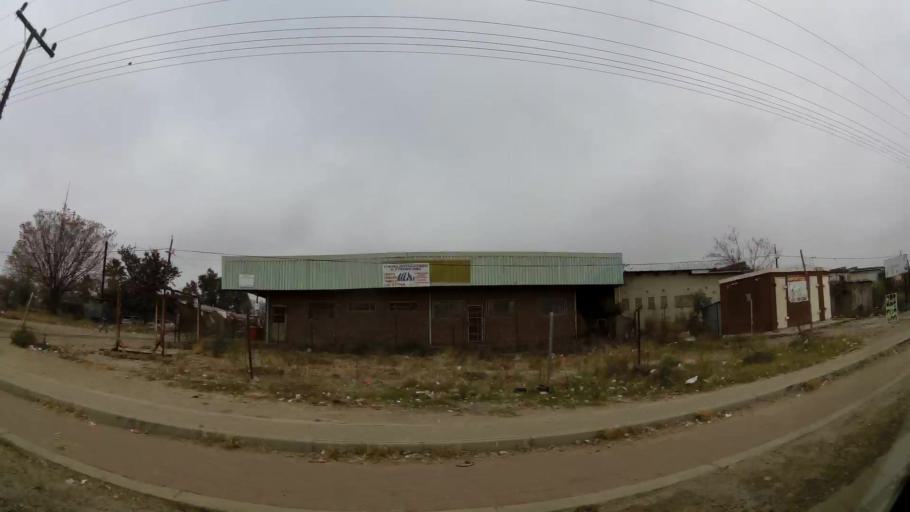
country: ZA
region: Limpopo
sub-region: Capricorn District Municipality
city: Polokwane
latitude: -23.8409
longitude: 29.3868
